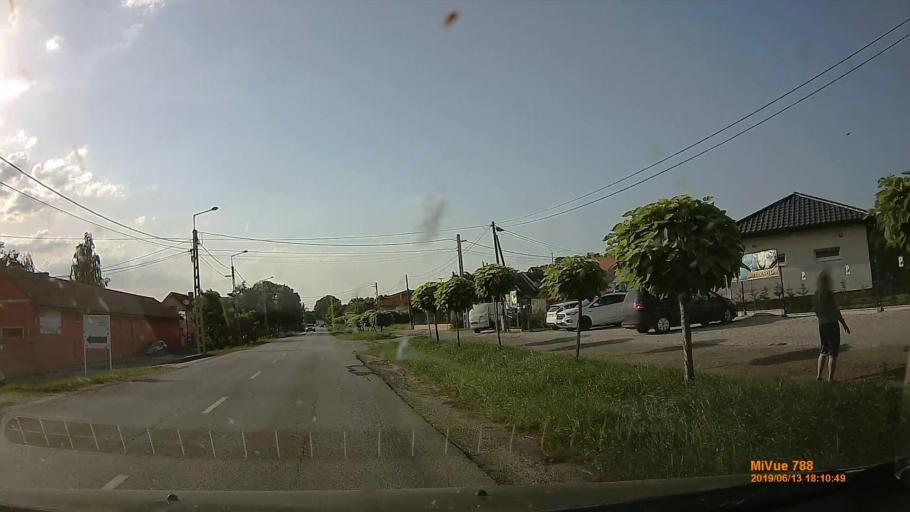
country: HU
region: Pest
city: Ecser
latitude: 47.4497
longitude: 19.3070
